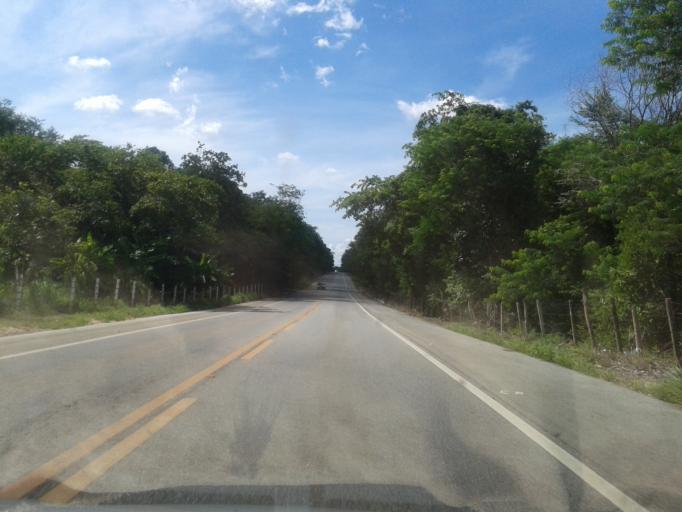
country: BR
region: Goias
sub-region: Itapuranga
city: Itapuranga
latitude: -15.4800
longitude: -50.3337
